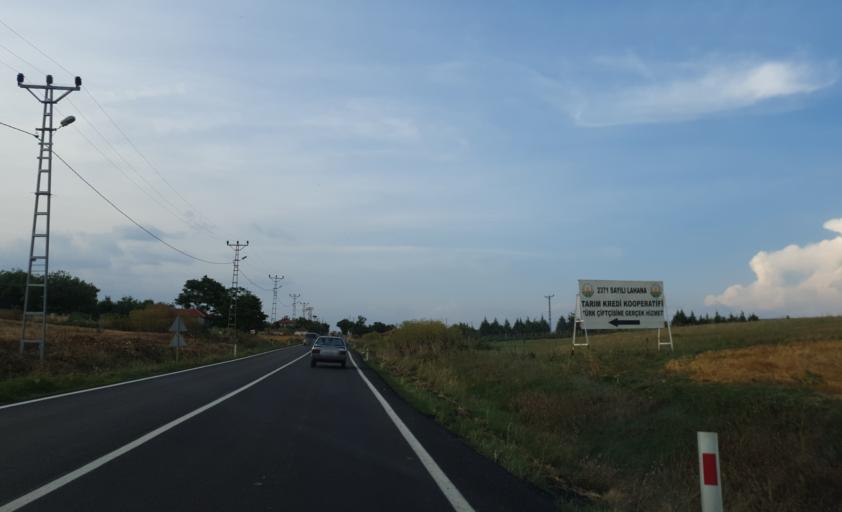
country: TR
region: Tekirdag
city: Hayrabolu
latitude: 41.2881
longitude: 27.1330
